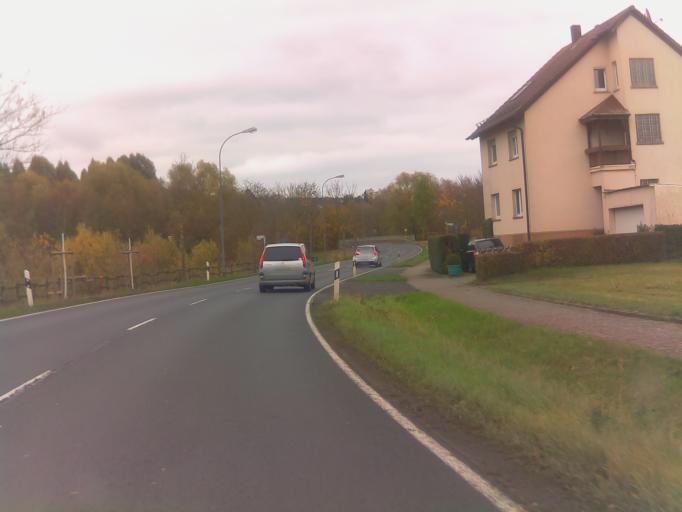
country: DE
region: Hesse
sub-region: Regierungsbezirk Kassel
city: Fulda
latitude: 50.5615
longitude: 9.6531
